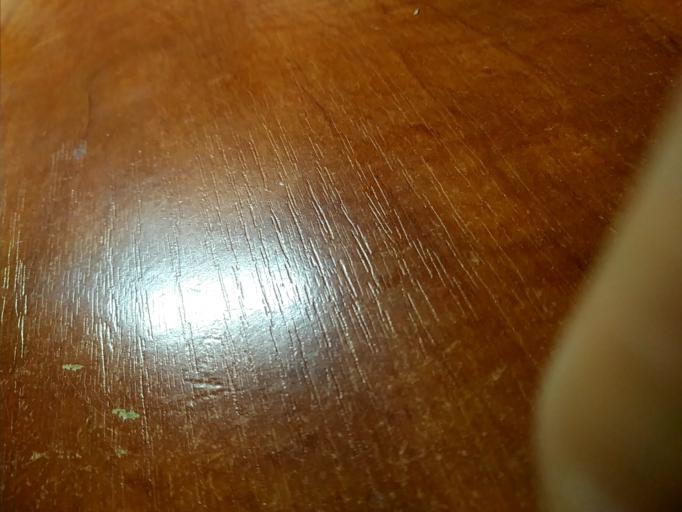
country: RU
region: Arkhangelskaya
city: Konevo
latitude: 62.5760
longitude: 38.6897
